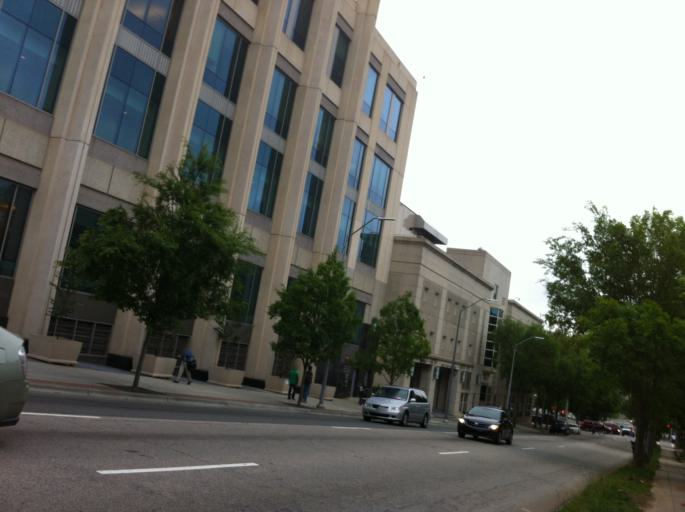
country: US
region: North Carolina
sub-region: Wake County
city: Raleigh
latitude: 35.7768
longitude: -78.6420
